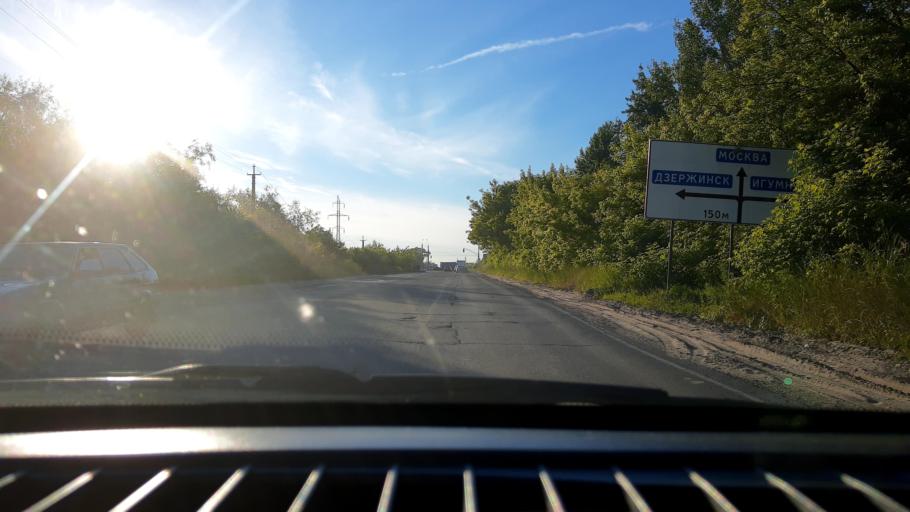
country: RU
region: Nizjnij Novgorod
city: Dzerzhinsk
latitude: 56.2491
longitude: 43.4980
